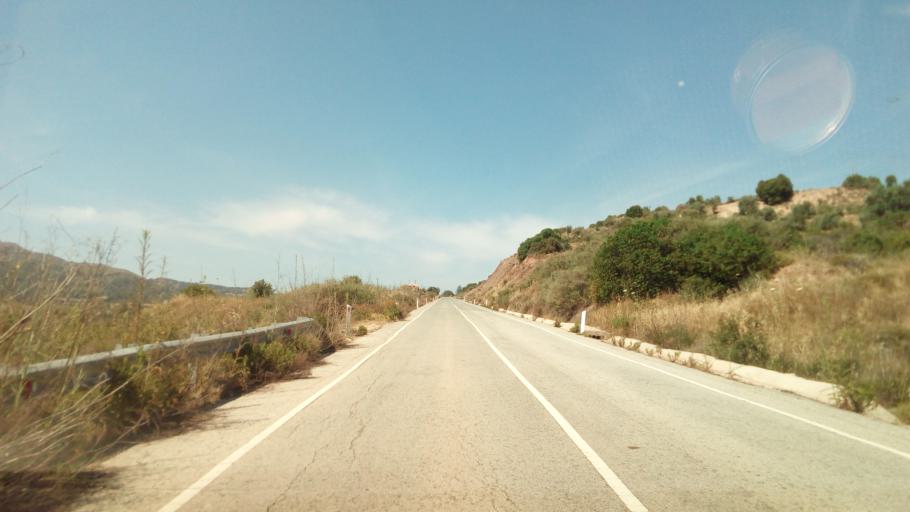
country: CY
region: Limassol
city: Pachna
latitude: 34.7948
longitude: 32.6984
